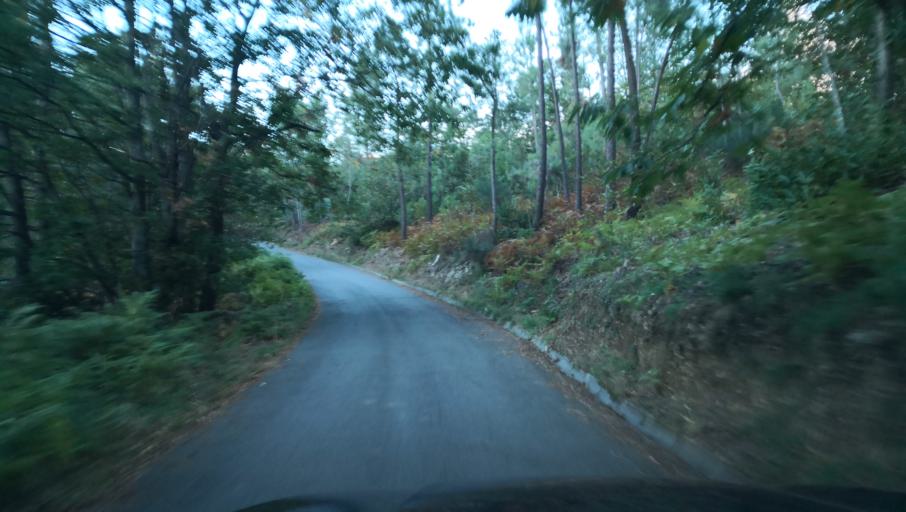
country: PT
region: Vila Real
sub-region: Santa Marta de Penaguiao
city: Santa Marta de Penaguiao
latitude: 41.2659
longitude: -7.8285
